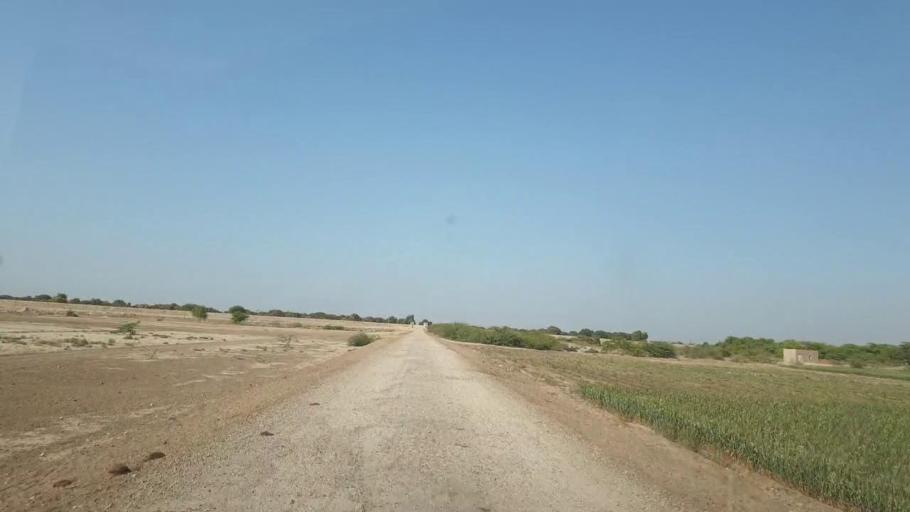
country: PK
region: Sindh
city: Nabisar
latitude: 25.0315
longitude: 69.4867
